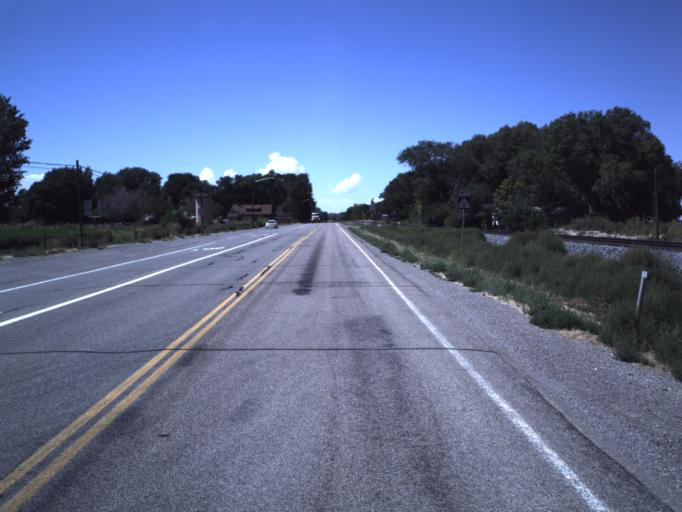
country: US
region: Utah
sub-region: Millard County
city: Delta
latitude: 39.5361
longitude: -112.2735
